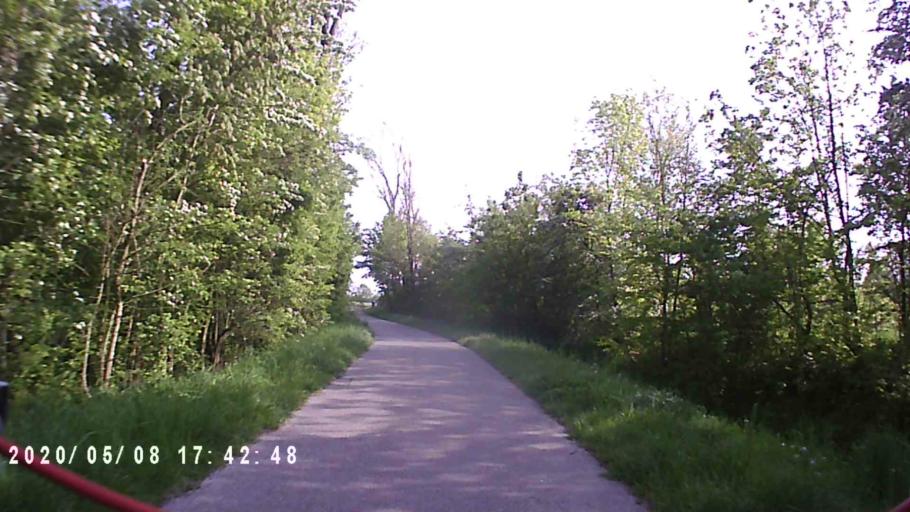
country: NL
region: Groningen
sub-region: Gemeente Winsum
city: Winsum
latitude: 53.3681
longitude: 6.5200
